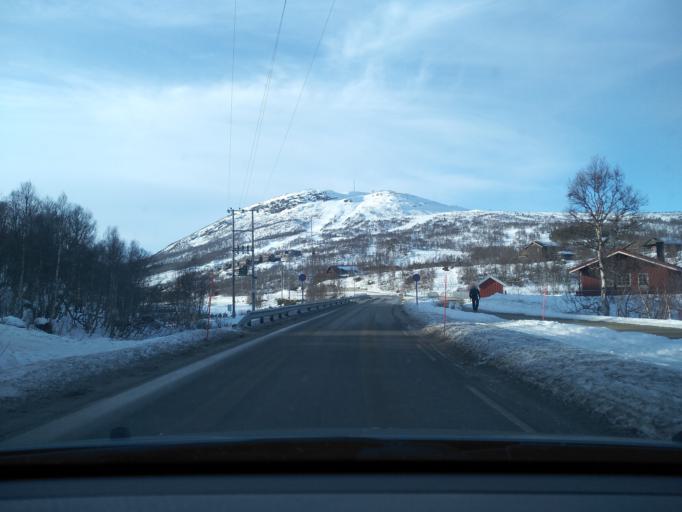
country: NO
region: Aust-Agder
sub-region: Bykle
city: Hovden
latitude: 59.5679
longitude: 7.3604
